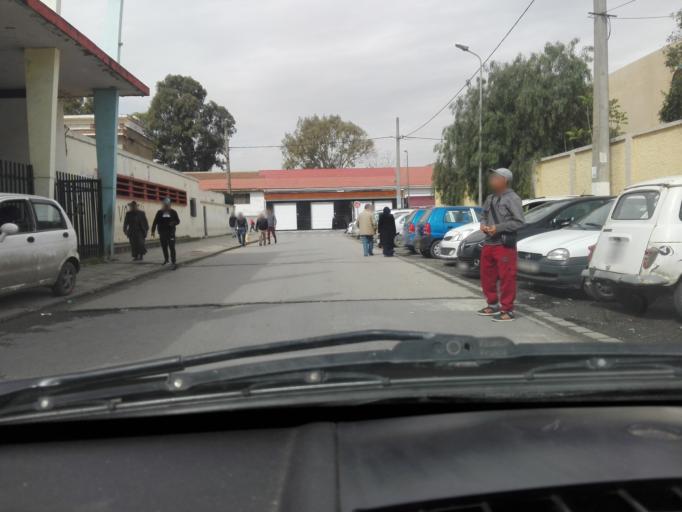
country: DZ
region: Alger
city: Bab Ezzouar
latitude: 36.7237
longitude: 3.1361
